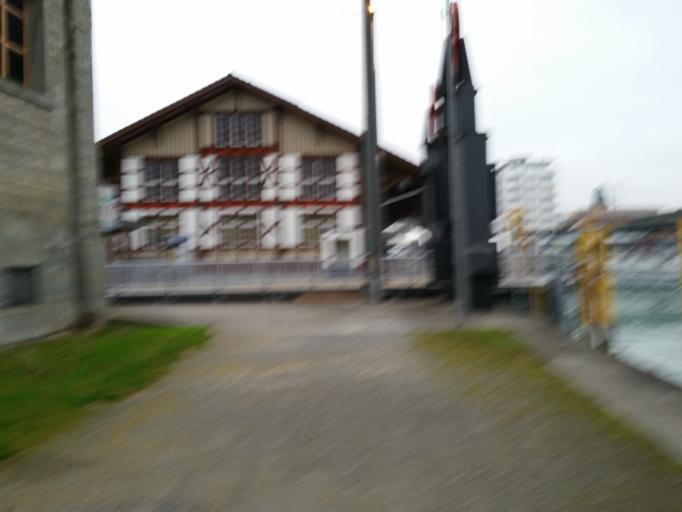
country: CH
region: Thurgau
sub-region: Arbon District
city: Romanshorn
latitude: 47.5647
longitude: 9.3814
